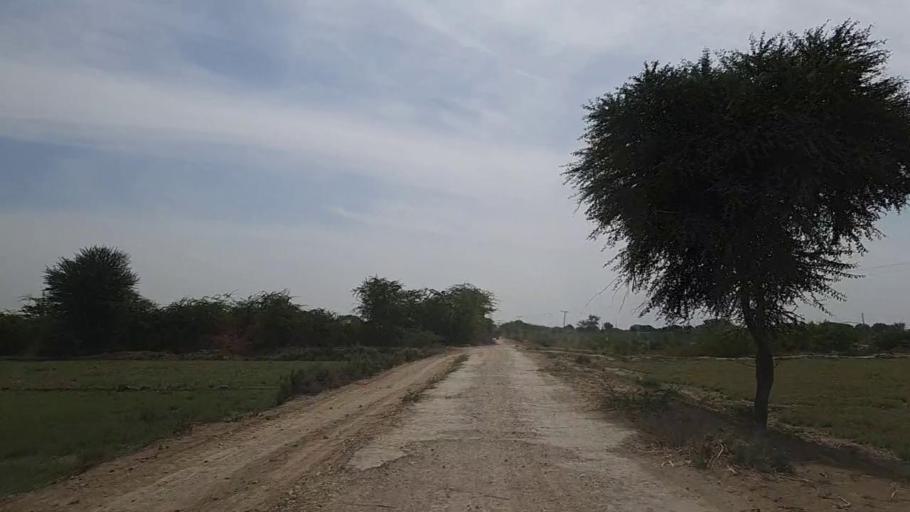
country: PK
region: Sindh
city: Samaro
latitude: 25.2674
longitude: 69.4536
